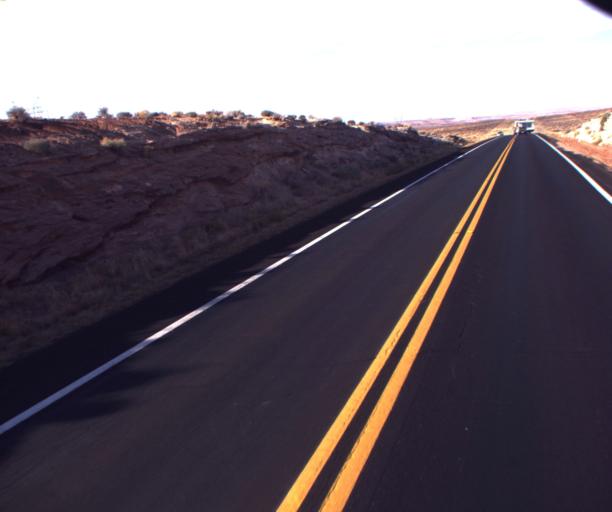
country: US
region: Arizona
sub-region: Apache County
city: Lukachukai
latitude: 36.9516
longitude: -109.5152
